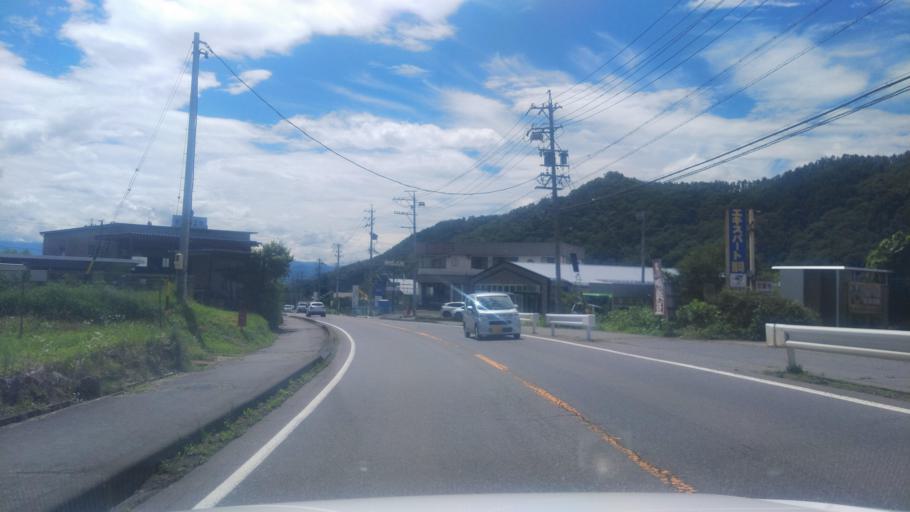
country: JP
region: Nagano
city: Ueda
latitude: 36.4352
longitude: 138.2993
